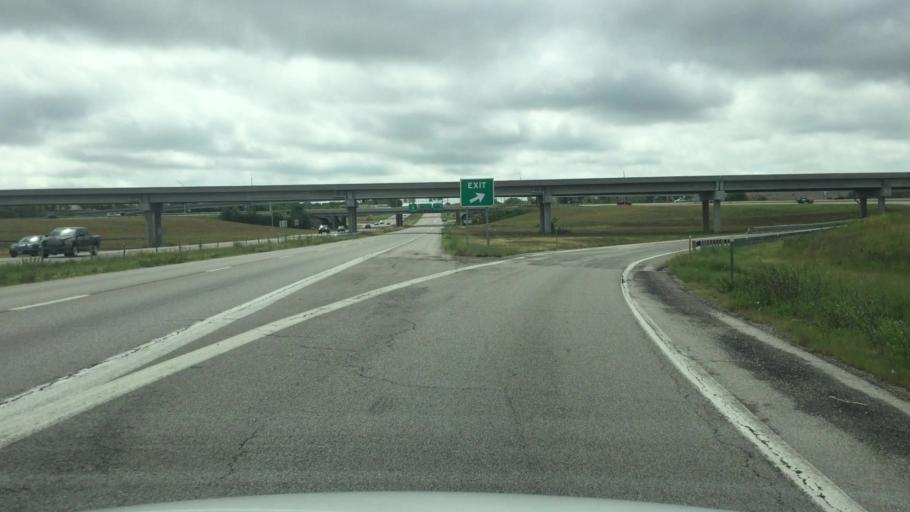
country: US
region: Missouri
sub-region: Jackson County
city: Lees Summit
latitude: 38.9375
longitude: -94.4075
